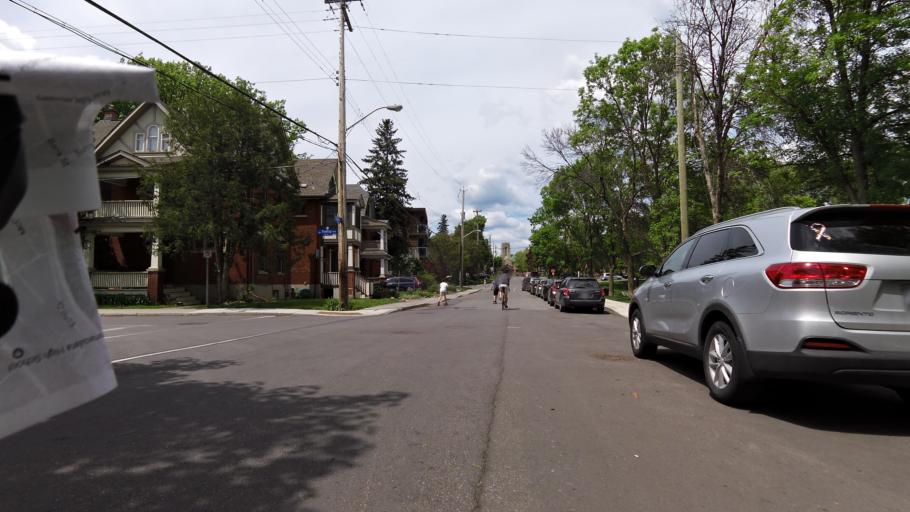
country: CA
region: Ontario
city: Ottawa
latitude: 45.3968
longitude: -75.6916
